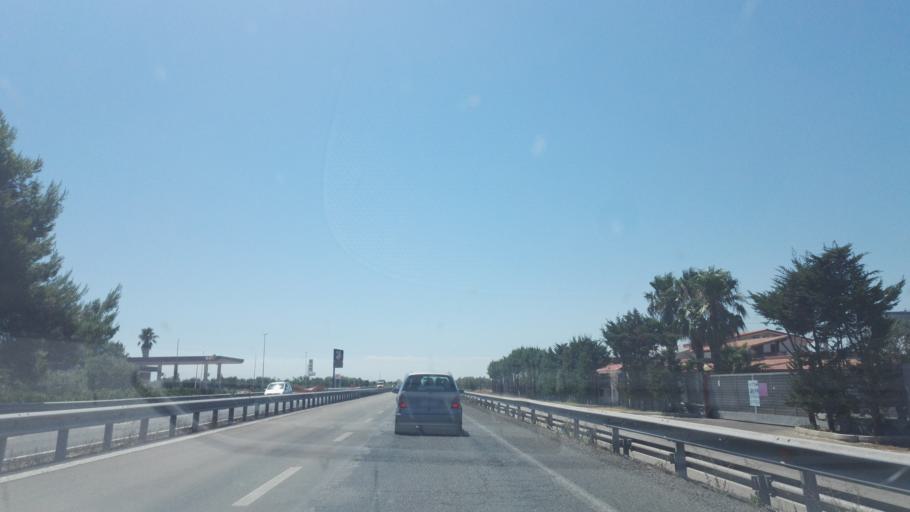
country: IT
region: Apulia
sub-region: Provincia di Taranto
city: Palagiano
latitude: 40.5167
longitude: 17.0083
